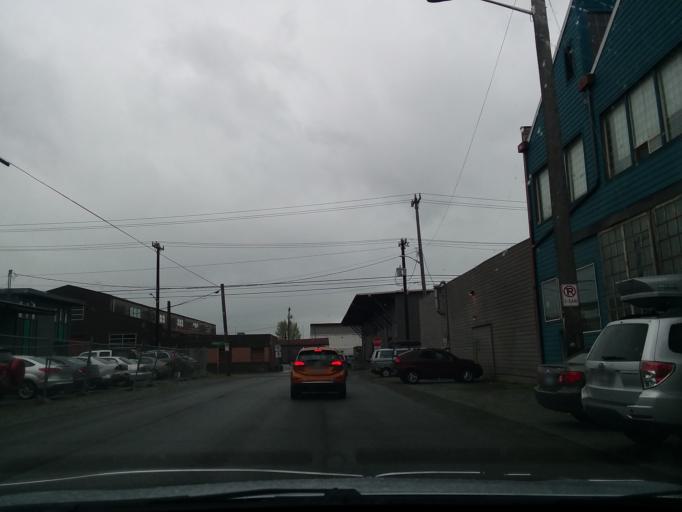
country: US
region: Washington
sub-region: King County
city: Seattle
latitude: 47.5749
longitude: -122.3333
